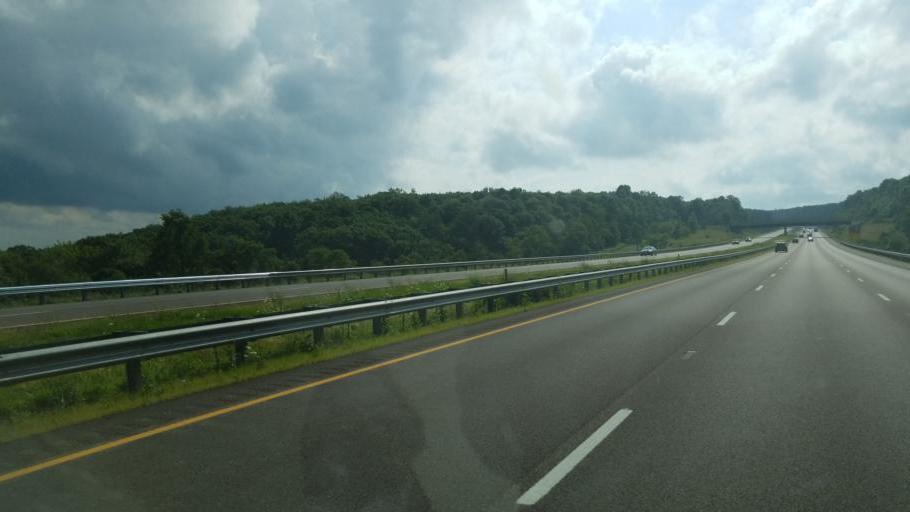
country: US
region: Pennsylvania
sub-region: Somerset County
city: Meyersdale
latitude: 39.6876
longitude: -79.1941
